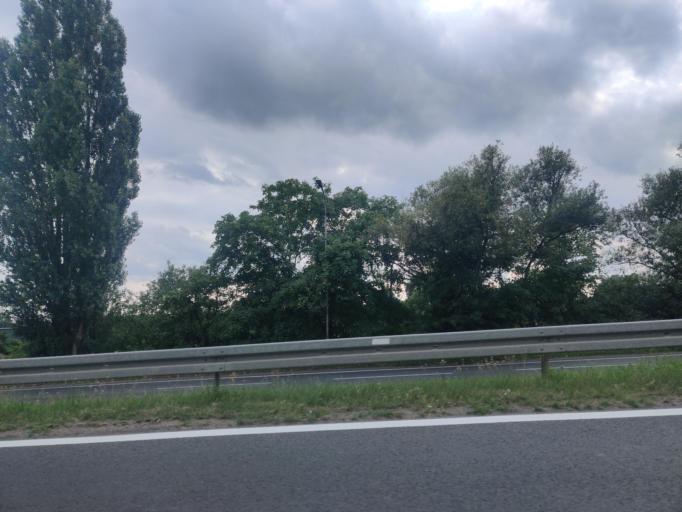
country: PL
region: Greater Poland Voivodeship
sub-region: Konin
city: Konin
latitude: 52.2090
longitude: 18.2643
